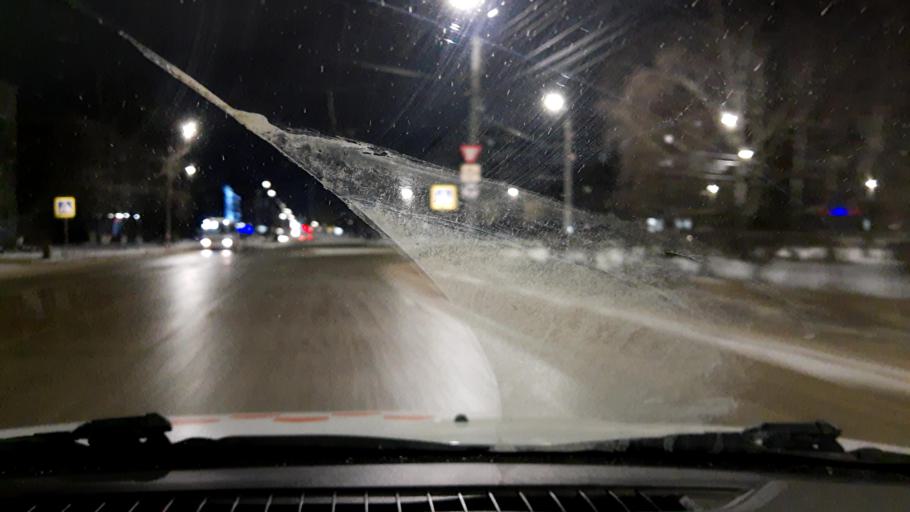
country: RU
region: Nizjnij Novgorod
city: Dzerzhinsk
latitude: 56.2302
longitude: 43.4571
